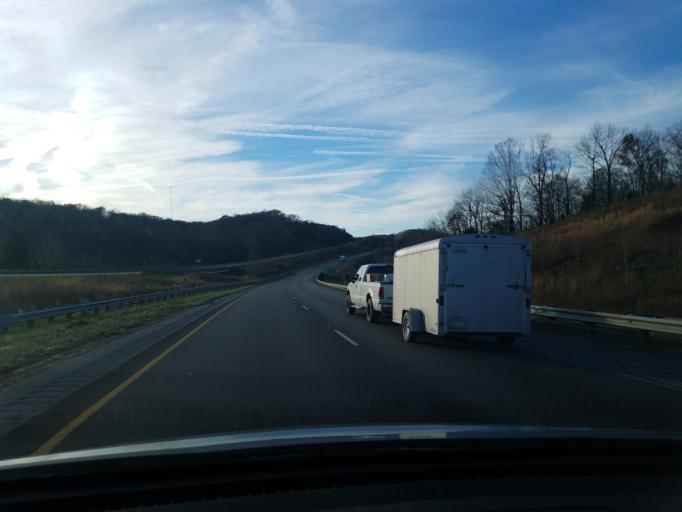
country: US
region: Indiana
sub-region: Crawford County
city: English
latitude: 38.2379
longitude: -86.5268
